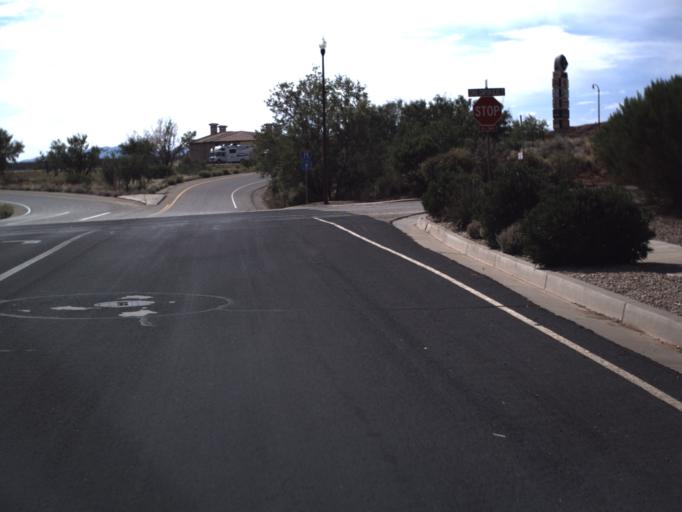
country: US
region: Utah
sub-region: Washington County
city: Washington
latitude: 37.1649
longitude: -113.4438
